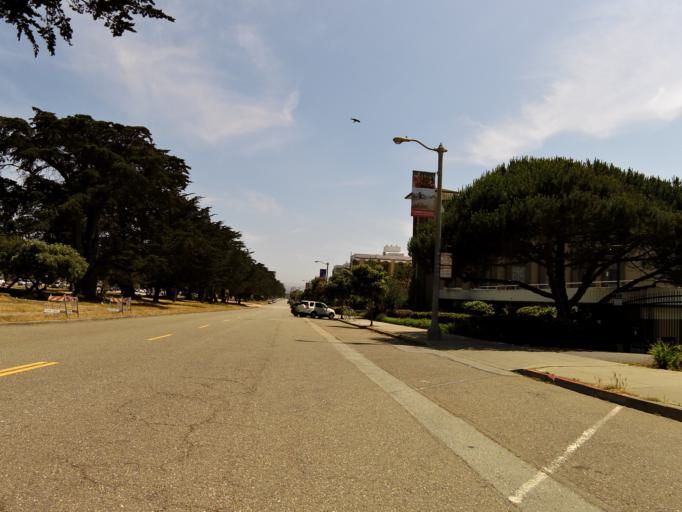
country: US
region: California
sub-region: San Mateo County
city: Daly City
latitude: 37.7494
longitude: -122.4955
